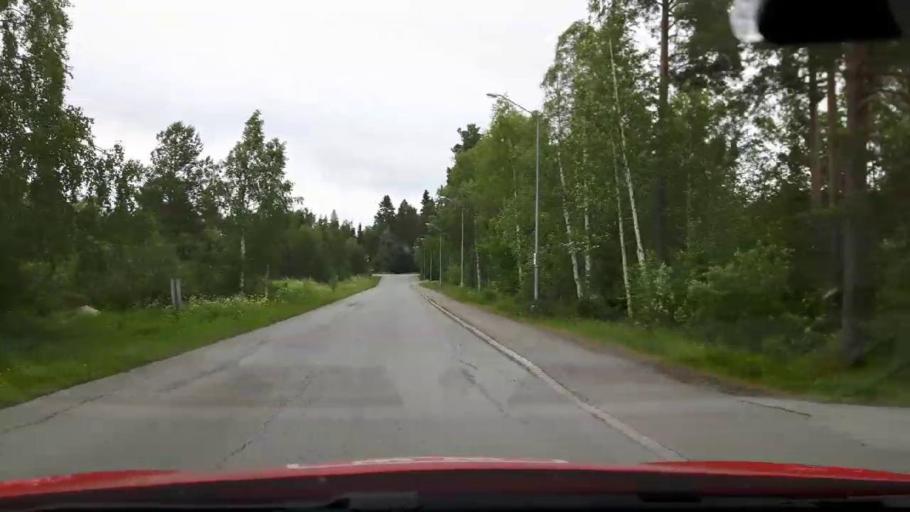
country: SE
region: Jaemtland
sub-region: OEstersunds Kommun
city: Ostersund
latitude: 63.2130
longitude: 14.6192
